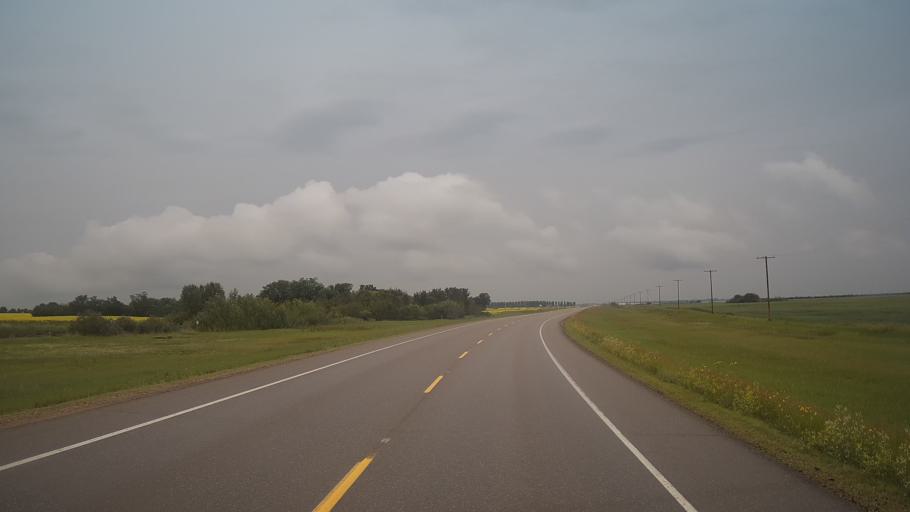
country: CA
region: Saskatchewan
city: Wilkie
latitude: 52.3334
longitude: -108.7135
